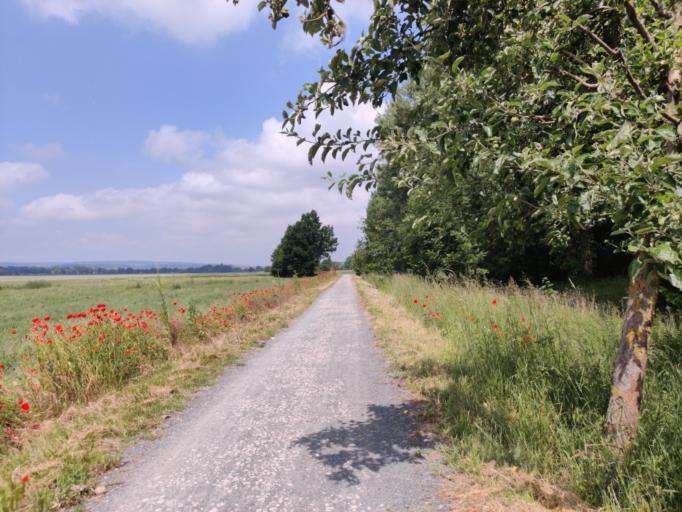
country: DE
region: Lower Saxony
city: Bad Salzdetfurth
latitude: 52.1049
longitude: 10.0044
